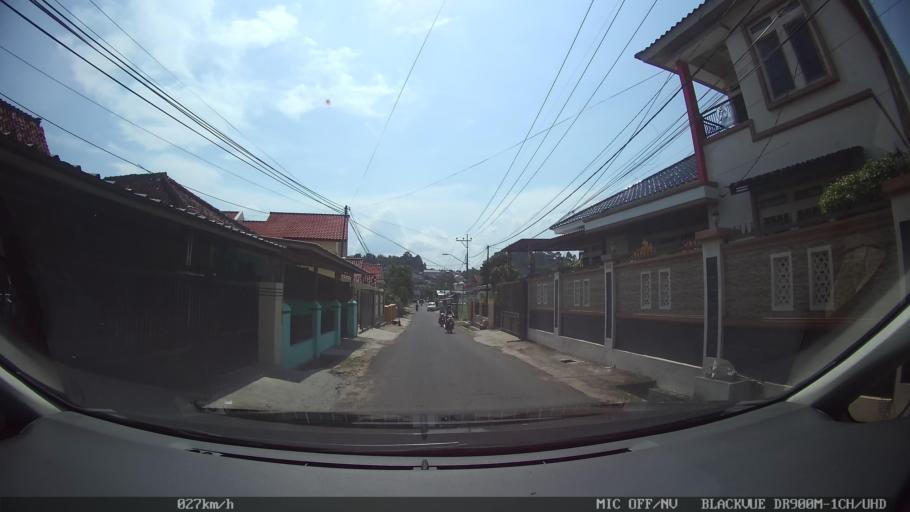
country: ID
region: Lampung
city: Kedaton
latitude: -5.3983
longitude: 105.2587
